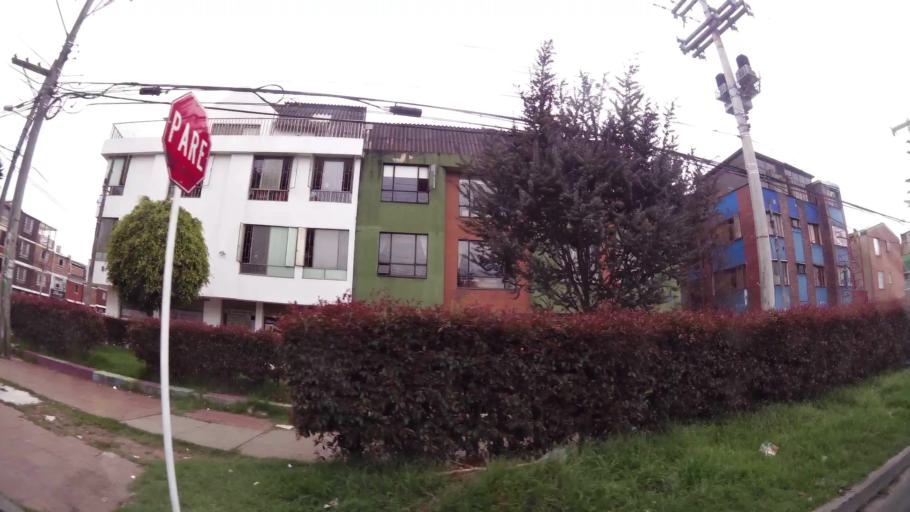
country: CO
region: Cundinamarca
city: Funza
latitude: 4.7181
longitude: -74.1257
